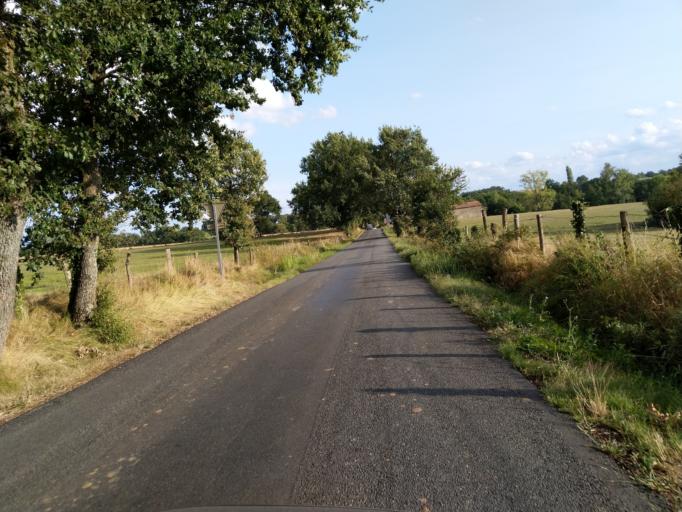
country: FR
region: Midi-Pyrenees
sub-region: Departement du Tarn
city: Frejairolles
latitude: 43.8780
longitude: 2.2339
